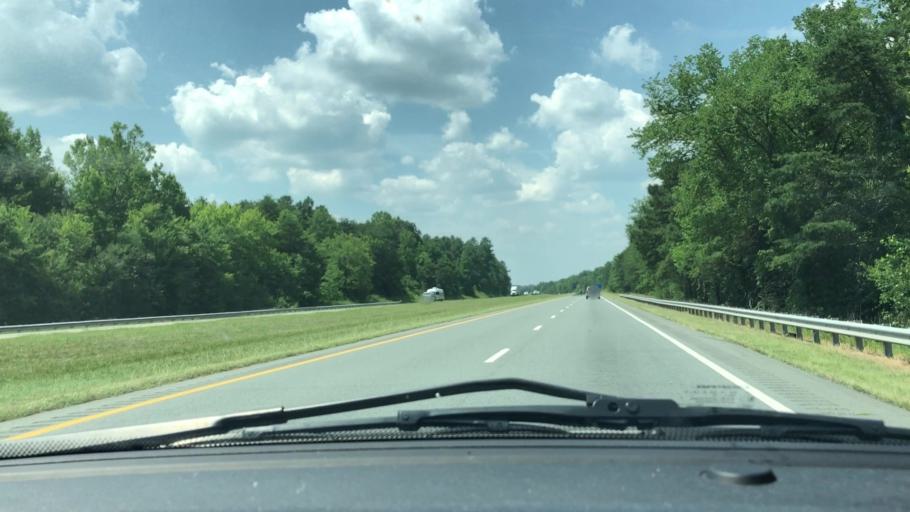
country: US
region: North Carolina
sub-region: Guilford County
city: Forest Oaks
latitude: 35.9464
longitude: -79.6888
